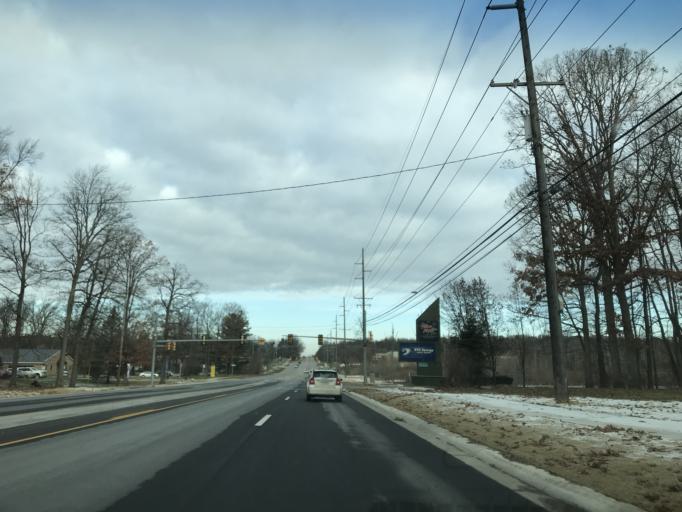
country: US
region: Michigan
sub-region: Oakland County
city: Clarkston
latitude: 42.7483
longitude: -83.3801
